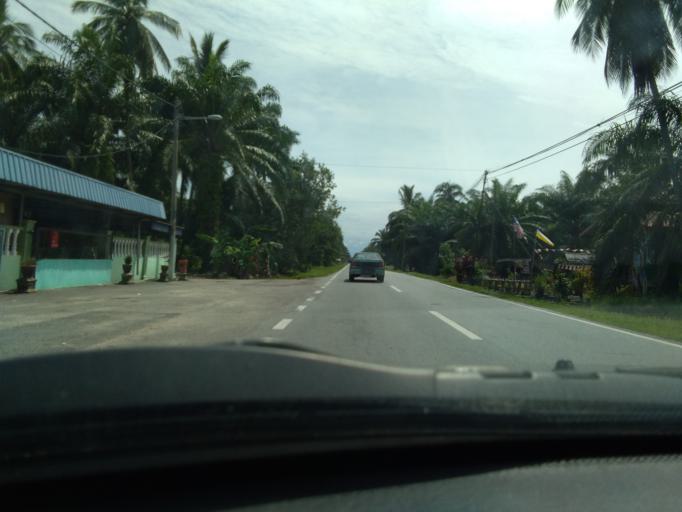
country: MY
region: Perak
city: Bagan Serai
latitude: 5.0361
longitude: 100.5677
